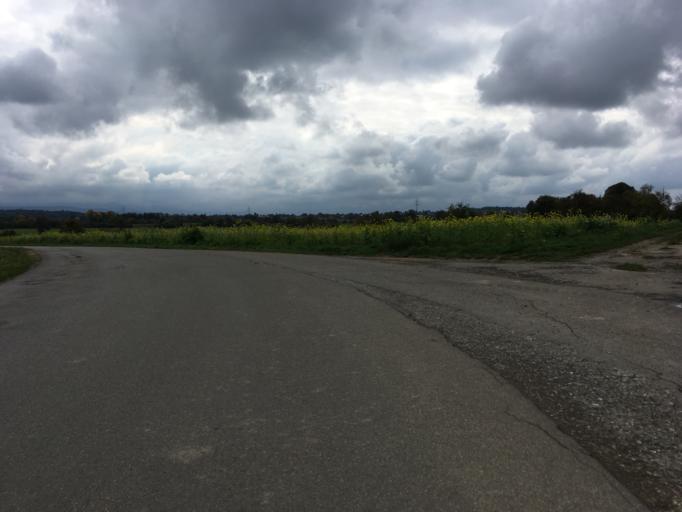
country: DE
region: Baden-Wuerttemberg
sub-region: Tuebingen Region
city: Kusterdingen
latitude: 48.5085
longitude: 9.1238
